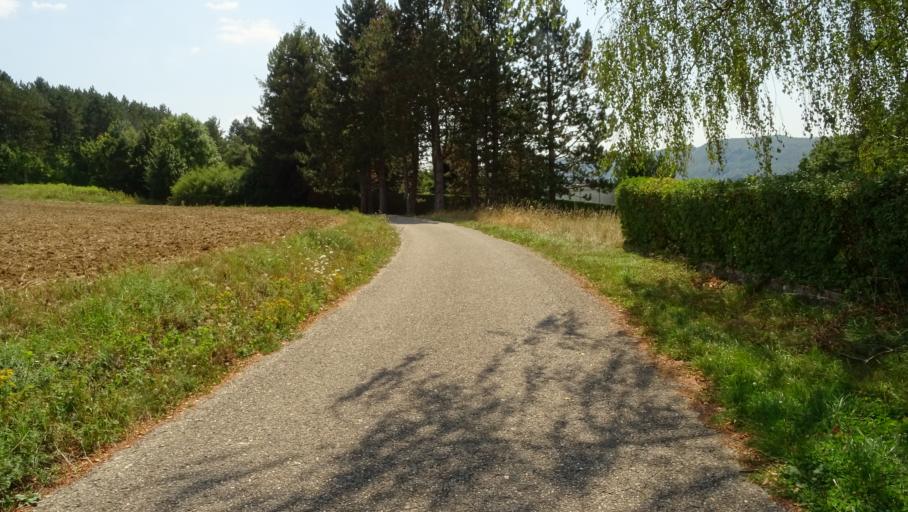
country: DE
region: Baden-Wuerttemberg
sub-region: Karlsruhe Region
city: Obrigheim
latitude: 49.3545
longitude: 9.1168
